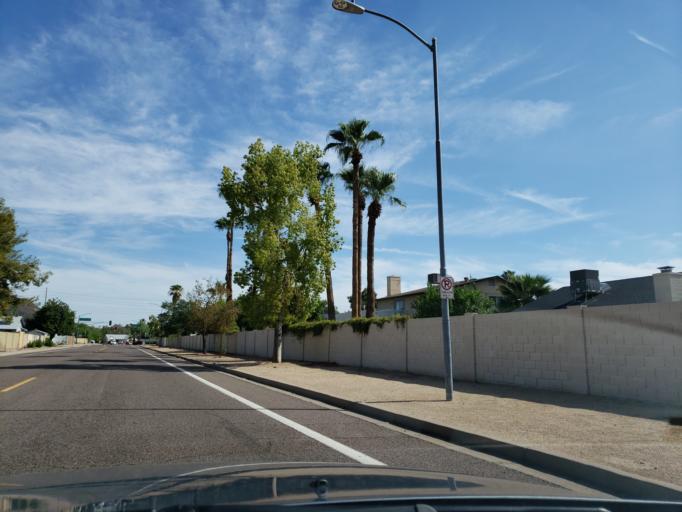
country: US
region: Arizona
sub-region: Maricopa County
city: Peoria
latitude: 33.6529
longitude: -112.1606
